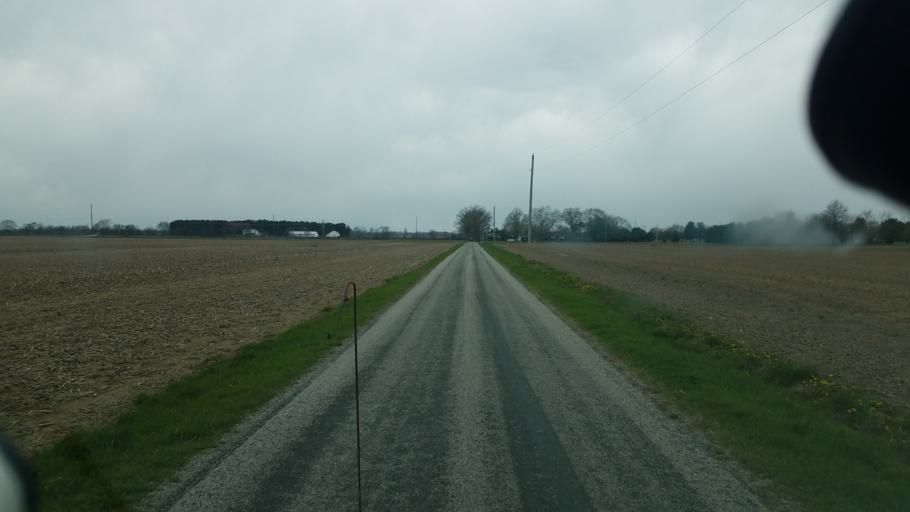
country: US
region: Ohio
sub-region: Marion County
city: Prospect
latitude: 40.4050
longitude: -83.1395
